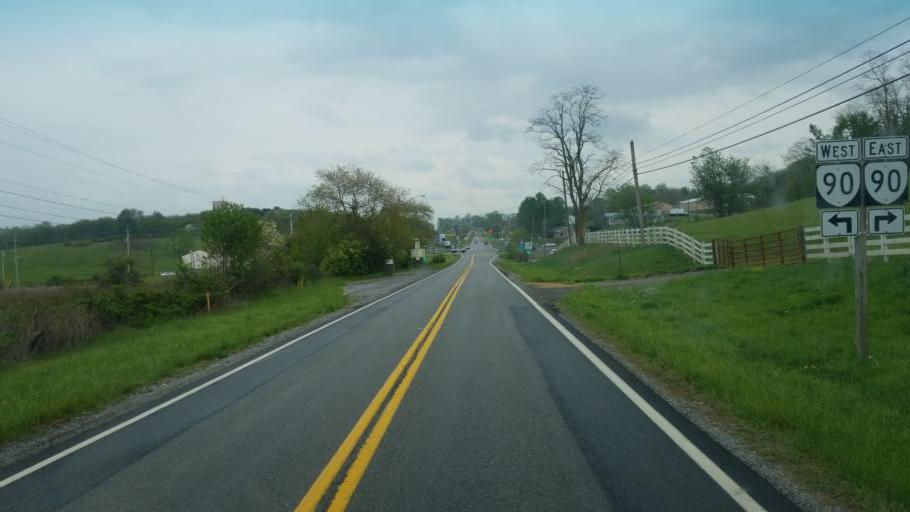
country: US
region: Virginia
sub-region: Wythe County
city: Rural Retreat
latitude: 36.9096
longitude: -81.2764
